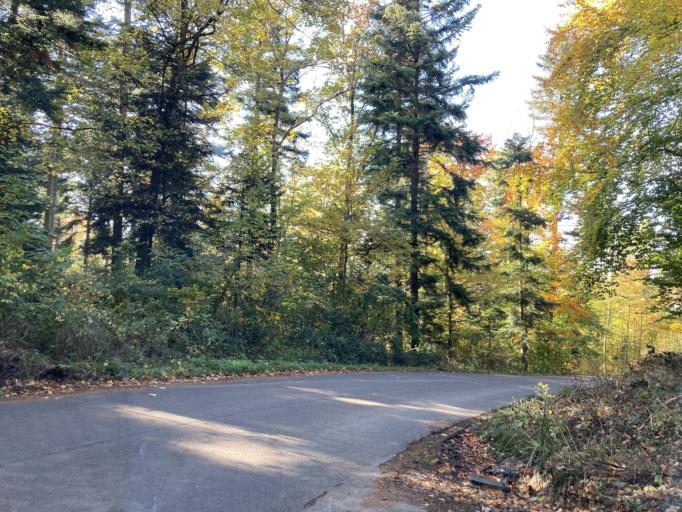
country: DE
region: Baden-Wuerttemberg
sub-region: Tuebingen Region
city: Mossingen
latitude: 48.3841
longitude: 9.0619
